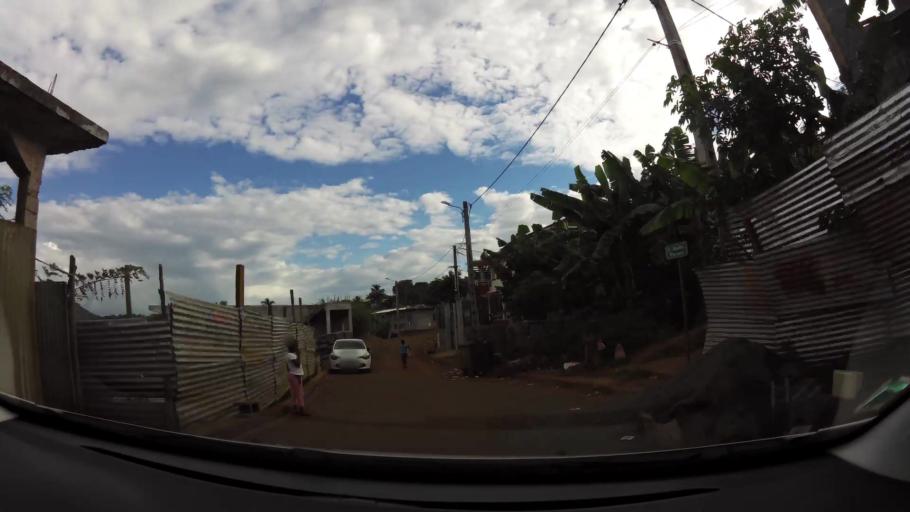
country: YT
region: Ouangani
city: Ouangani
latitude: -12.8405
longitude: 45.1338
